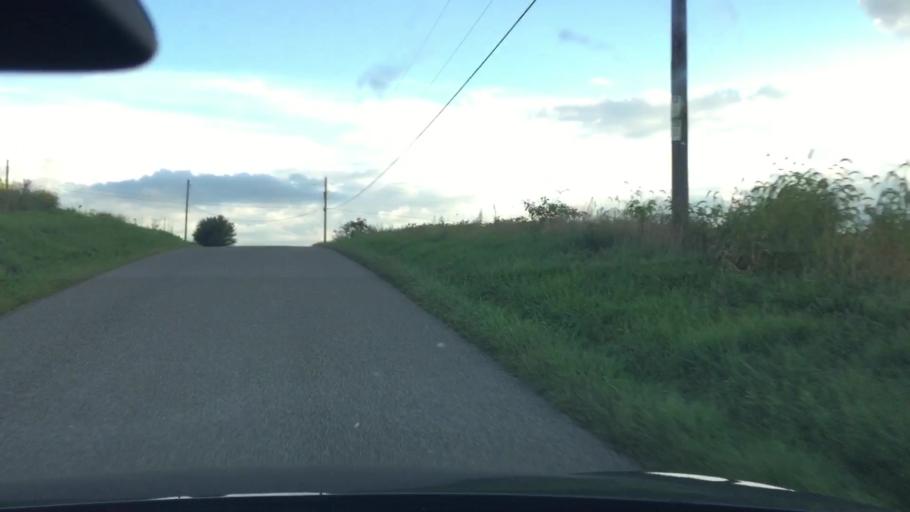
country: US
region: Pennsylvania
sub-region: Butler County
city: Oak Hills
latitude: 40.8141
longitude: -79.8916
